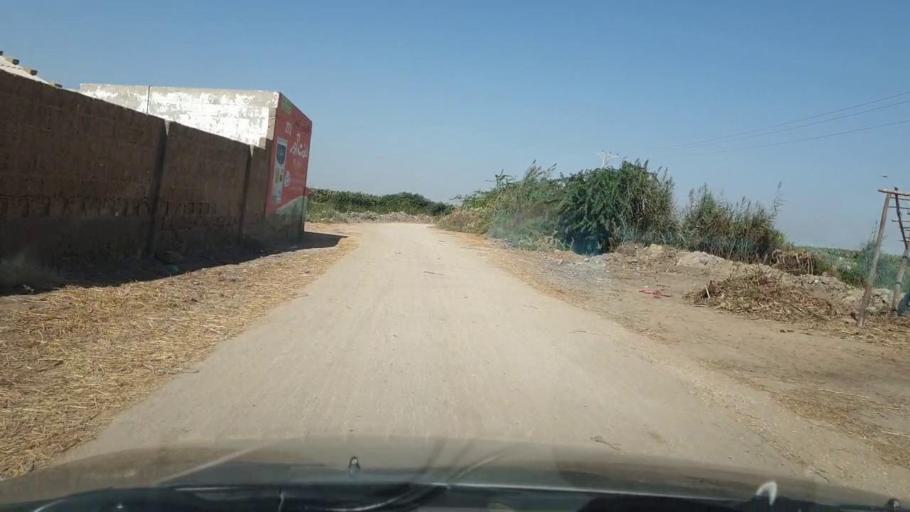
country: PK
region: Sindh
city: Thatta
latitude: 24.6393
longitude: 67.8933
